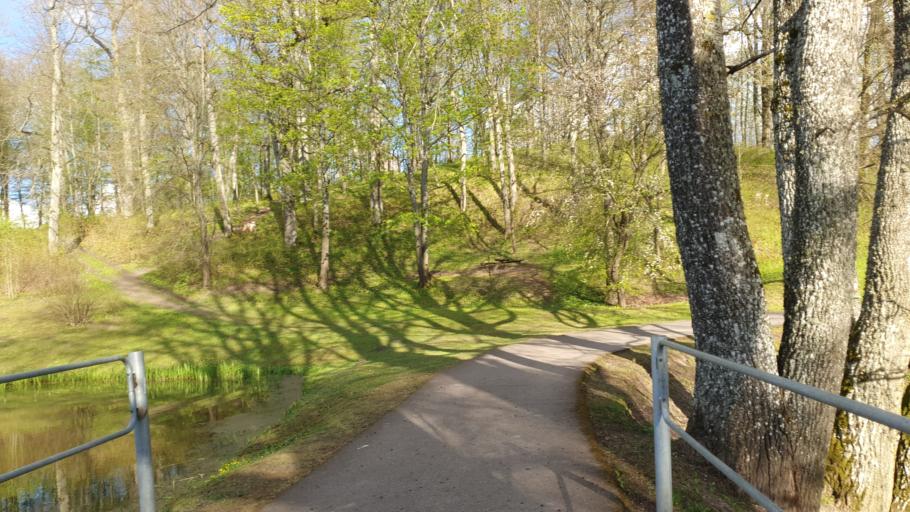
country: LT
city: Gelgaudiskis
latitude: 55.0989
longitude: 22.9884
